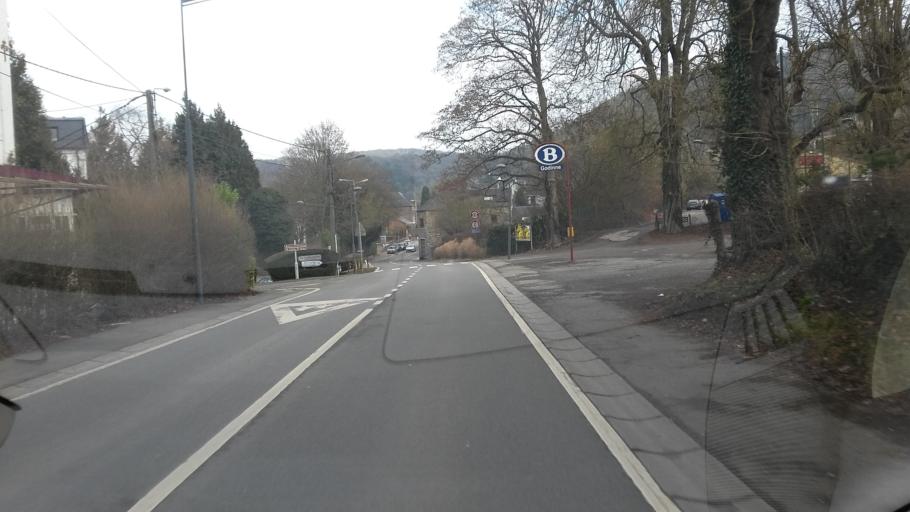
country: BE
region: Wallonia
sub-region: Province de Namur
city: Yvoir
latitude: 50.3491
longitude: 4.8682
